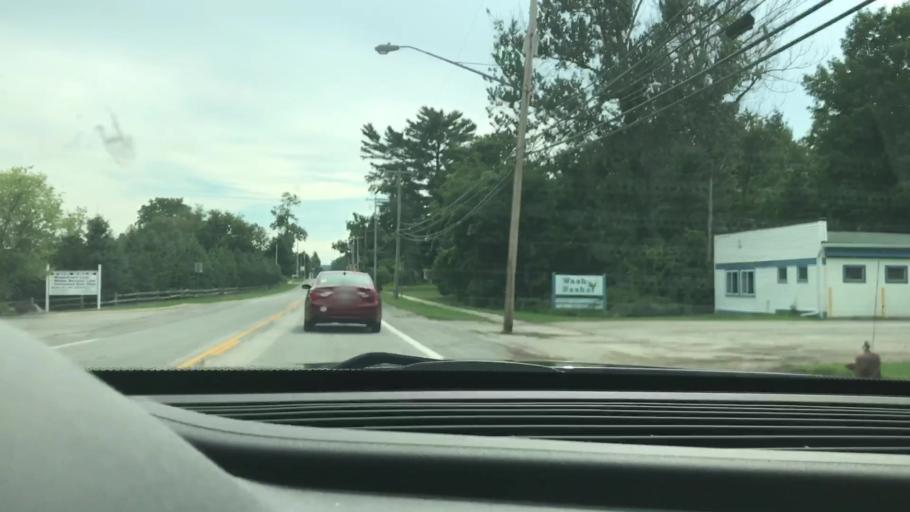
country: US
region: Michigan
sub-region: Antrim County
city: Bellaire
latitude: 45.0752
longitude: -85.2642
